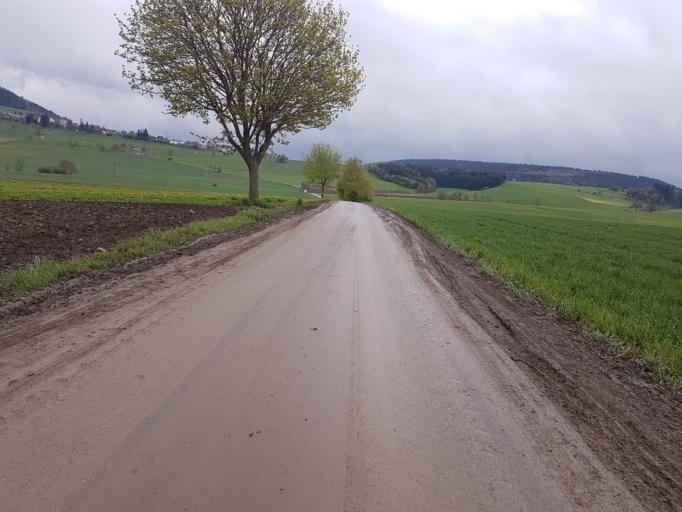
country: DE
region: Baden-Wuerttemberg
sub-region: Freiburg Region
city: Hufingen
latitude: 47.9007
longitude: 8.5402
